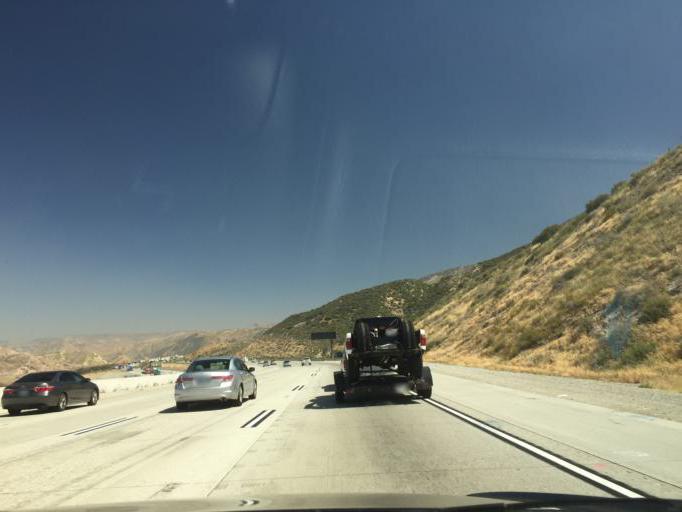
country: US
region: California
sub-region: San Bernardino County
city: Oak Hills
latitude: 34.2724
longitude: -117.4494
